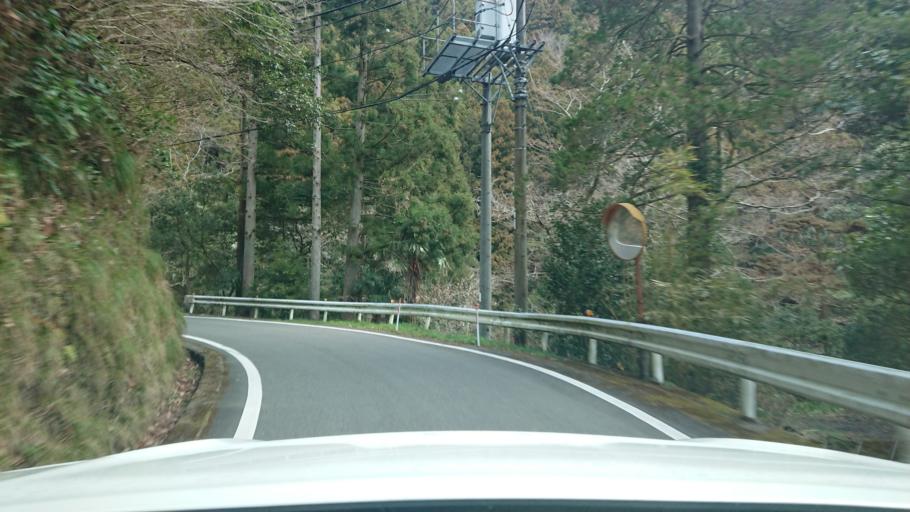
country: JP
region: Tokushima
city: Ishii
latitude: 33.9059
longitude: 134.3964
